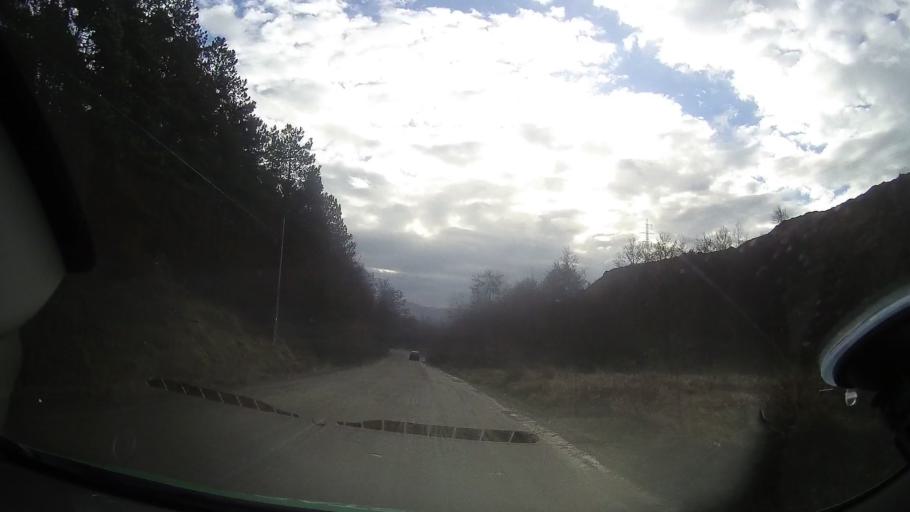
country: RO
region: Cluj
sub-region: Comuna Baisoara
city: Baisoara
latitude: 46.5858
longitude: 23.4600
